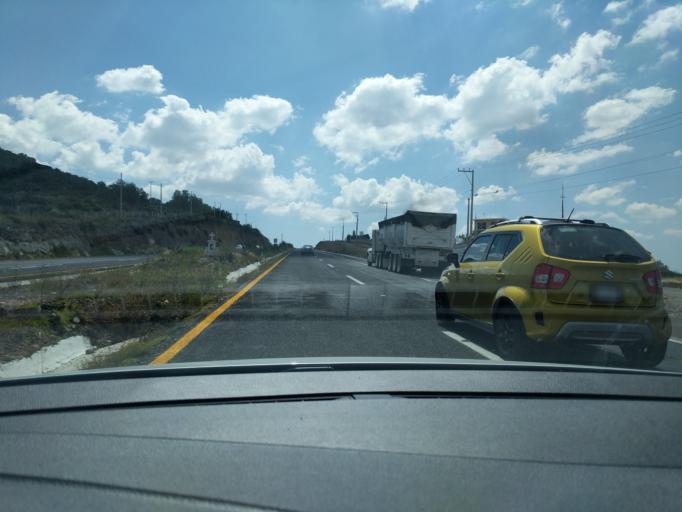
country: MX
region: Hidalgo
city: Zempoala
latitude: 19.8938
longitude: -98.6700
